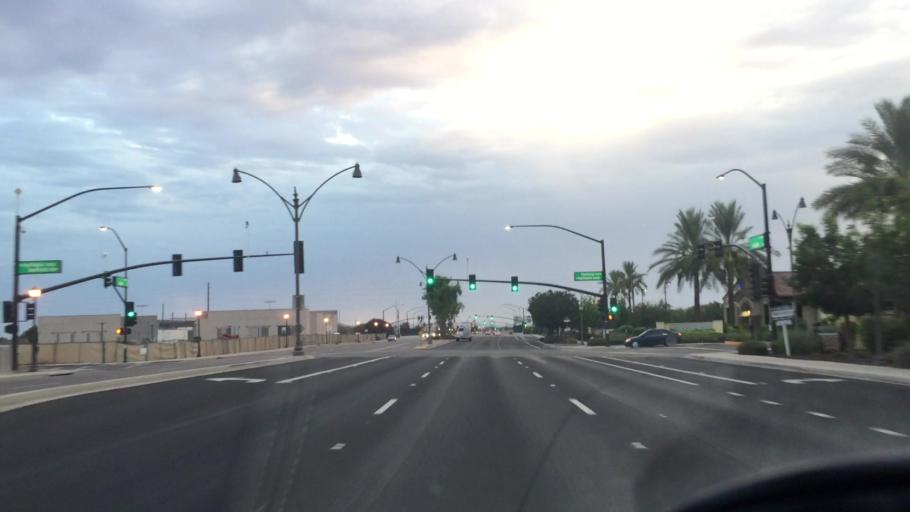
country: US
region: Arizona
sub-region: Maricopa County
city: Gilbert
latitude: 33.3245
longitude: -111.7211
